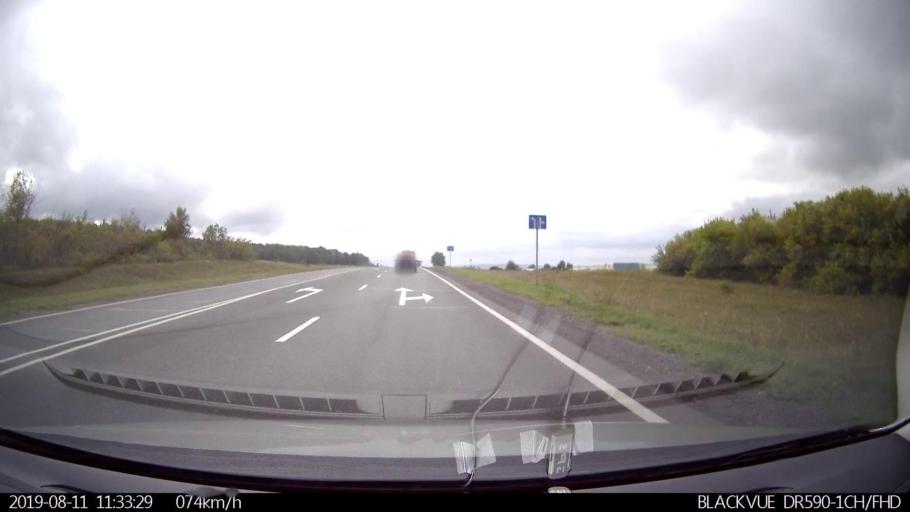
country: RU
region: Ulyanovsk
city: Krasnyy Gulyay
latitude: 54.0268
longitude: 48.2130
